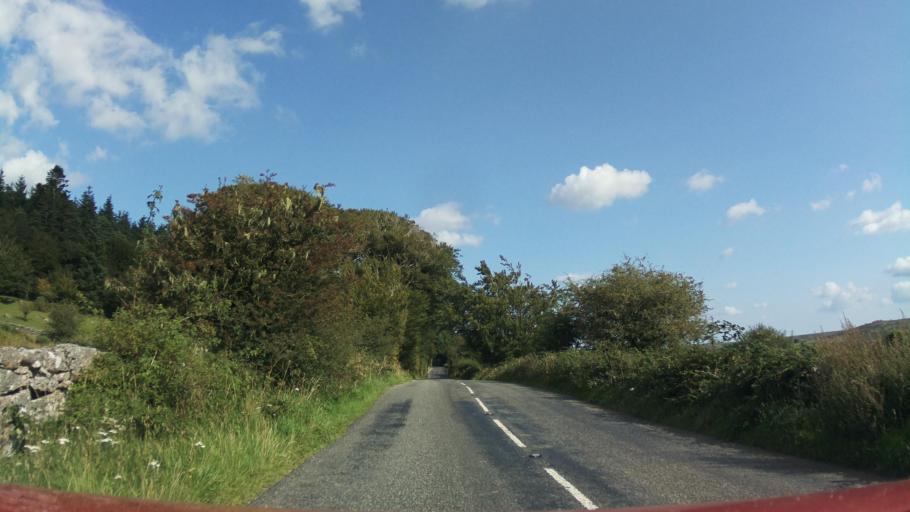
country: GB
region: England
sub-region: Devon
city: Buckfastleigh
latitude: 50.5467
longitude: -3.8934
